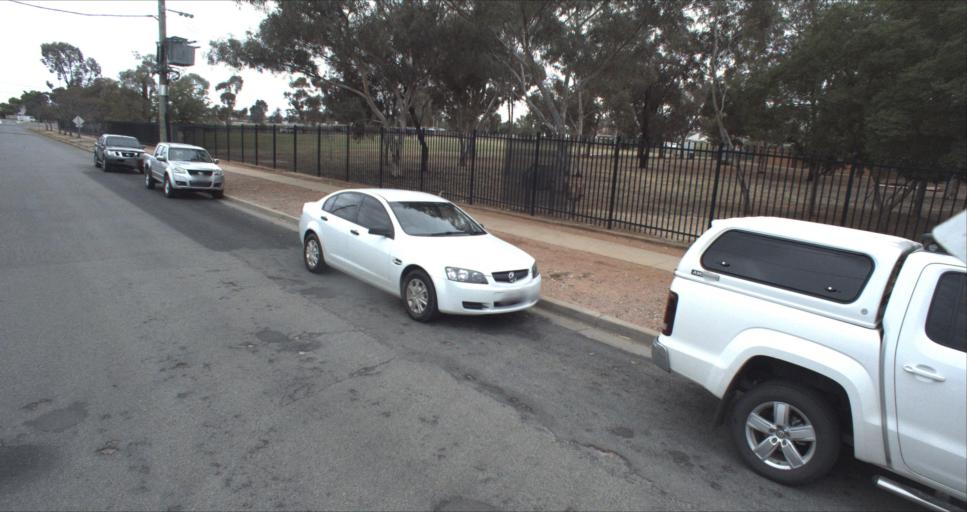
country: AU
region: New South Wales
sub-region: Leeton
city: Leeton
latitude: -34.5468
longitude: 146.4042
